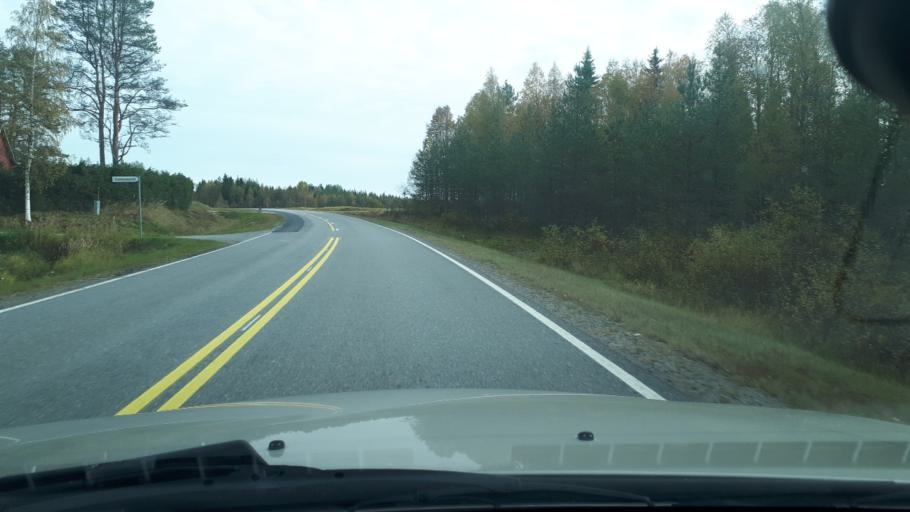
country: FI
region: Lapland
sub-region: Rovaniemi
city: Ranua
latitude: 66.0006
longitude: 26.2392
